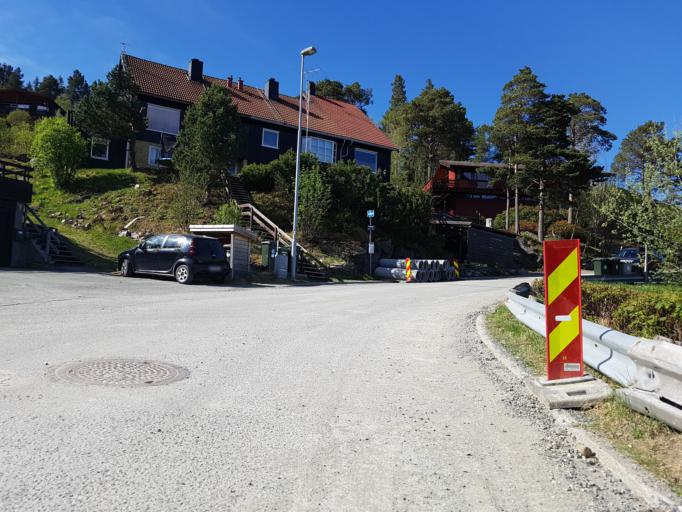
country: NO
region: Sor-Trondelag
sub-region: Trondheim
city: Trondheim
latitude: 63.4500
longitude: 10.3016
